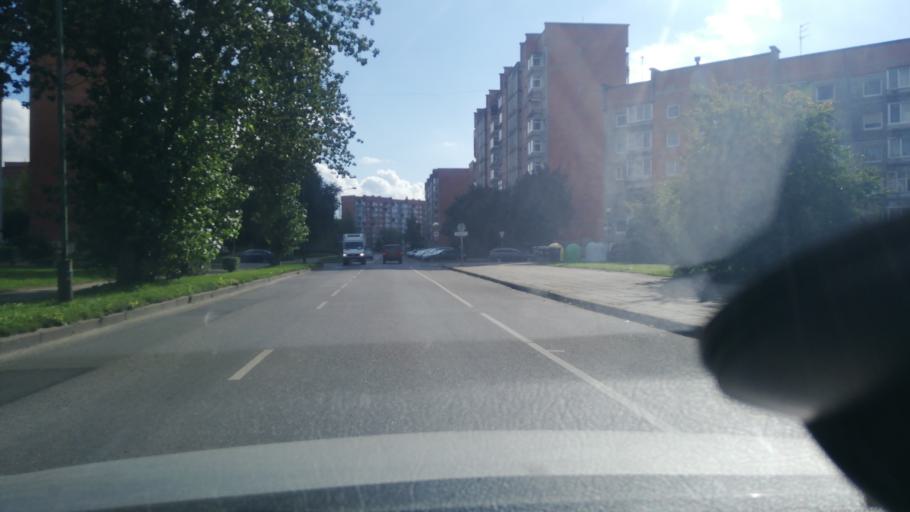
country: LT
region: Klaipedos apskritis
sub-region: Klaipeda
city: Klaipeda
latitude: 55.6699
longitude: 21.1998
